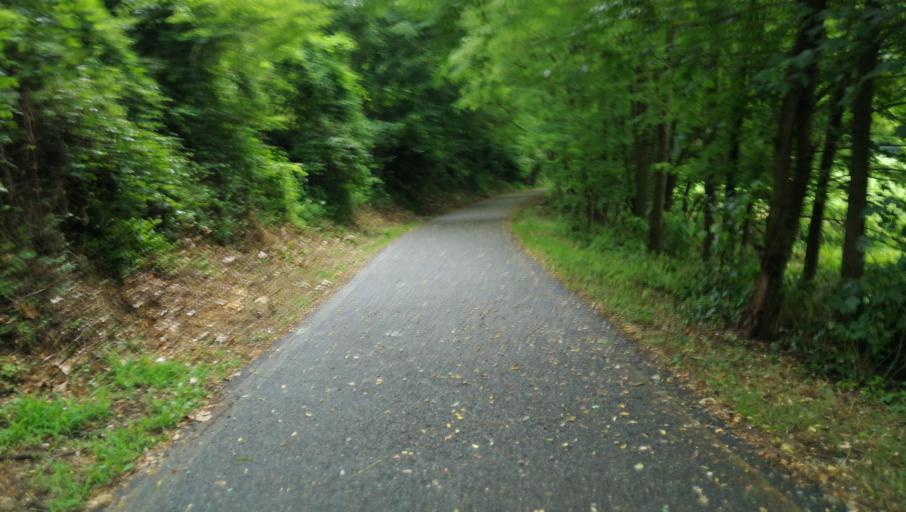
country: IT
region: Lombardy
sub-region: Provincia di Varese
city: Cittiglio
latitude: 45.8952
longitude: 8.6527
